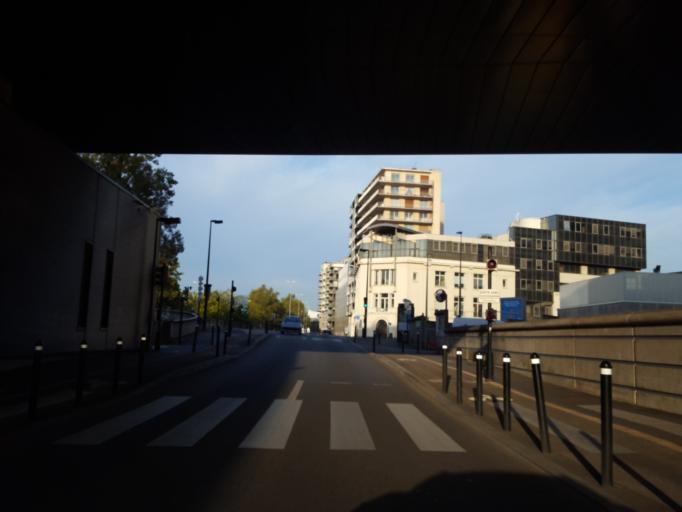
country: FR
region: Pays de la Loire
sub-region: Departement de la Loire-Atlantique
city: Nantes
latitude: 47.2093
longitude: -1.5545
